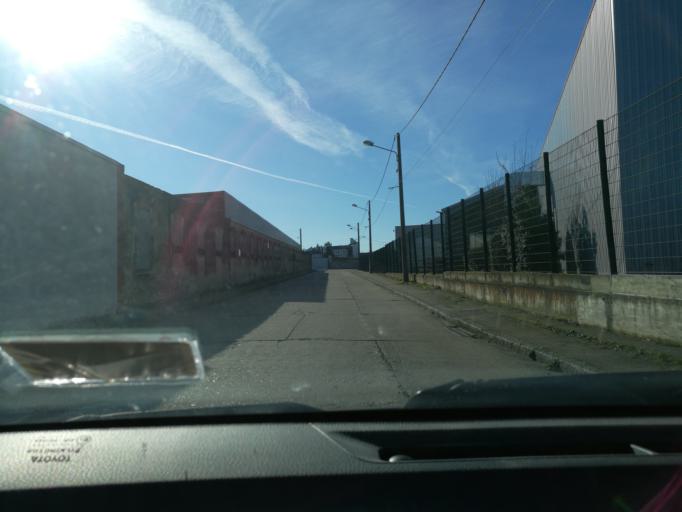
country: FR
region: Centre
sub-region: Departement du Loiret
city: Orleans
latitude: 47.9131
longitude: 1.8857
